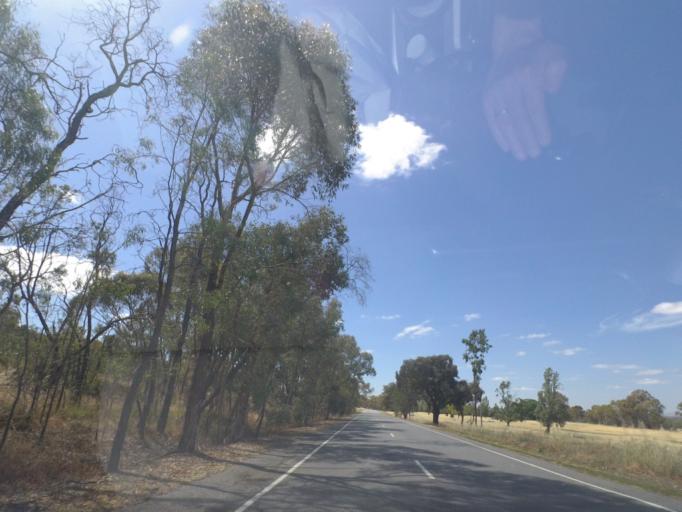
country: AU
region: Victoria
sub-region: Wangaratta
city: Wangaratta
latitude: -36.4536
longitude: 146.2374
